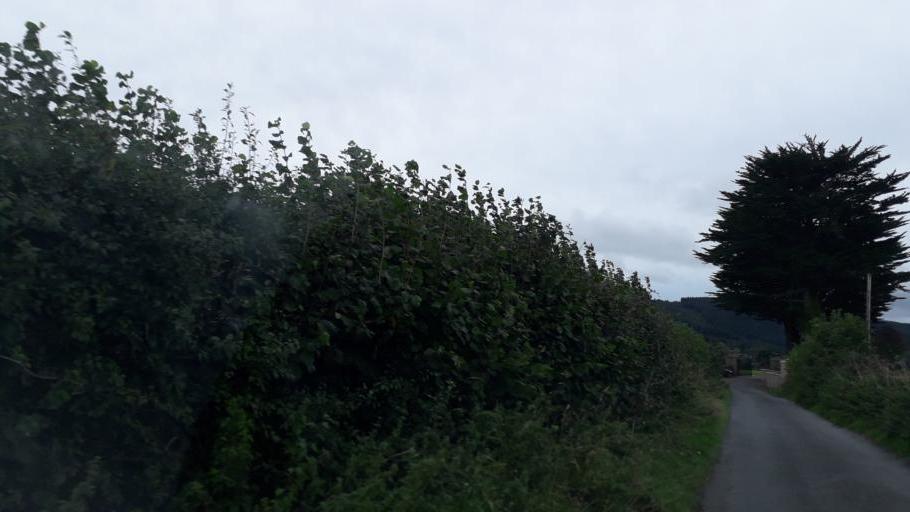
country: IE
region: Leinster
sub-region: Wicklow
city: Enniskerry
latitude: 53.1742
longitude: -6.2031
